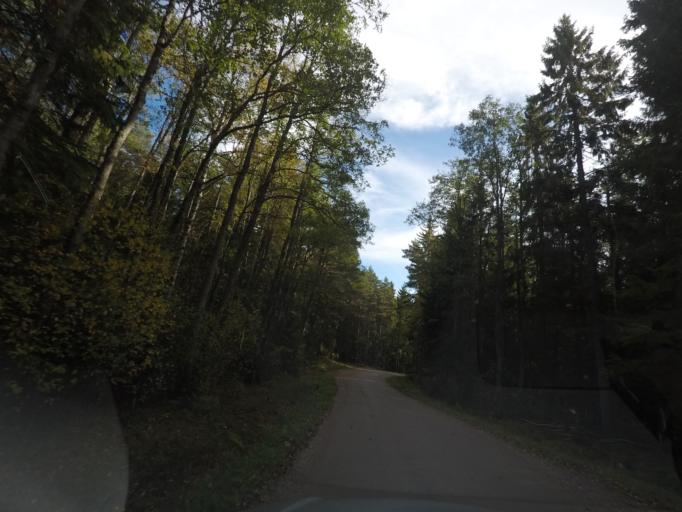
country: SE
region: Vaestmanland
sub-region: Kungsors Kommun
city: Kungsoer
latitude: 59.3332
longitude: 16.2206
